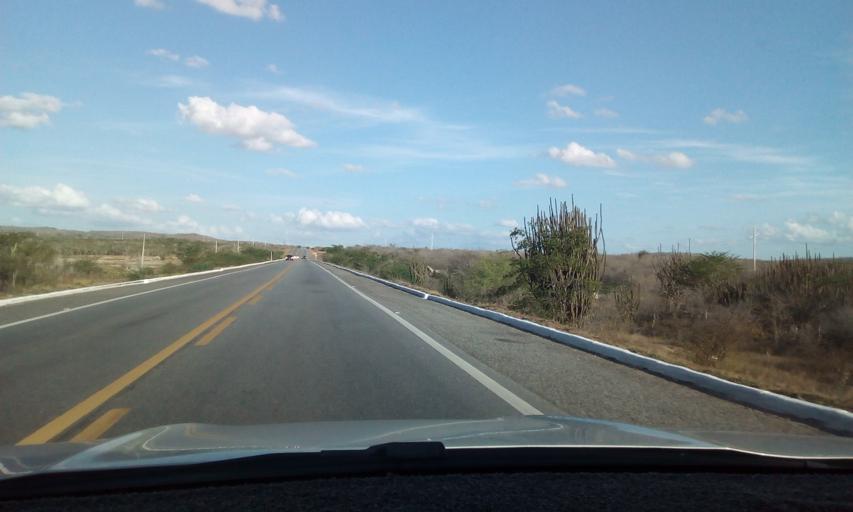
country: BR
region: Paraiba
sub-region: Pocinhos
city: Pocinhos
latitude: -7.1468
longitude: -36.1280
